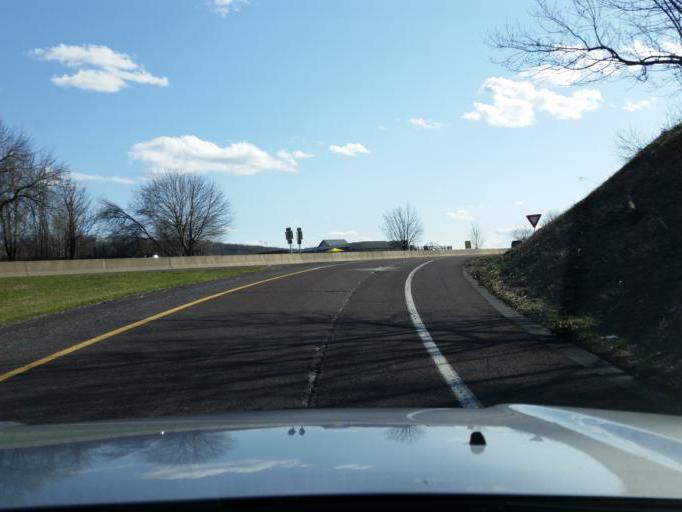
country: US
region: Pennsylvania
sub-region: Dauphin County
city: Hummelstown
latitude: 40.2655
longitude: -76.6884
